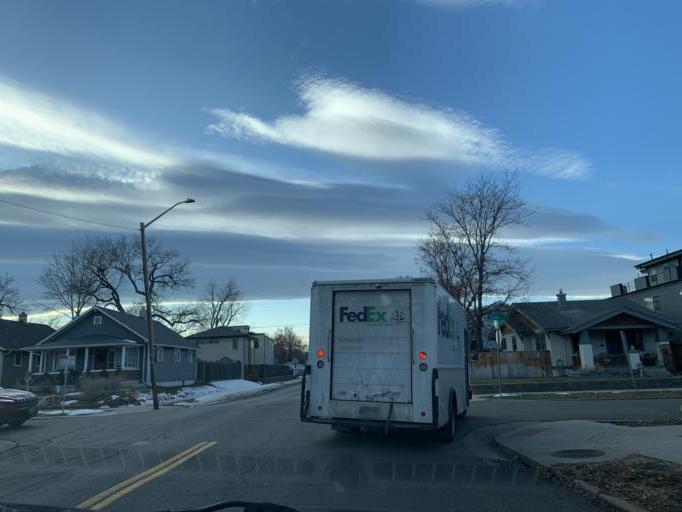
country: US
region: Colorado
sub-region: Jefferson County
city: Edgewater
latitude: 39.7766
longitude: -105.0460
